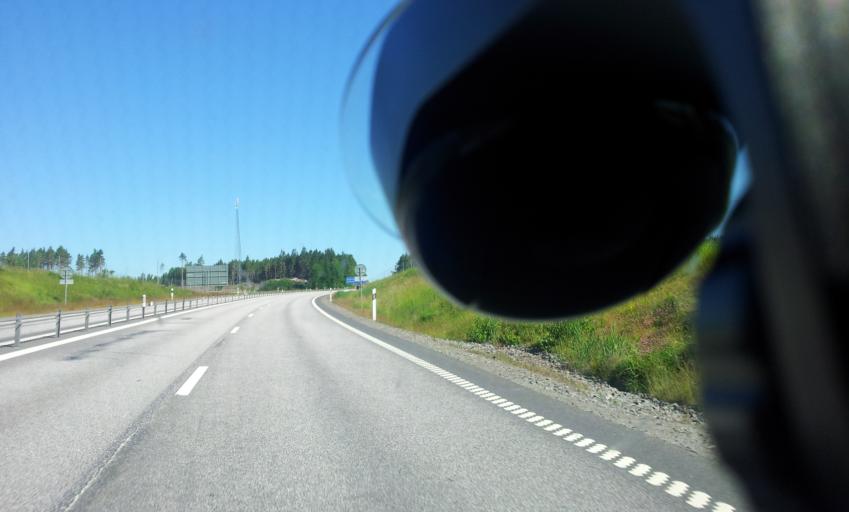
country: SE
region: OEstergoetland
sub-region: Valdemarsviks Kommun
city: Gusum
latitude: 58.3369
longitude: 16.4528
